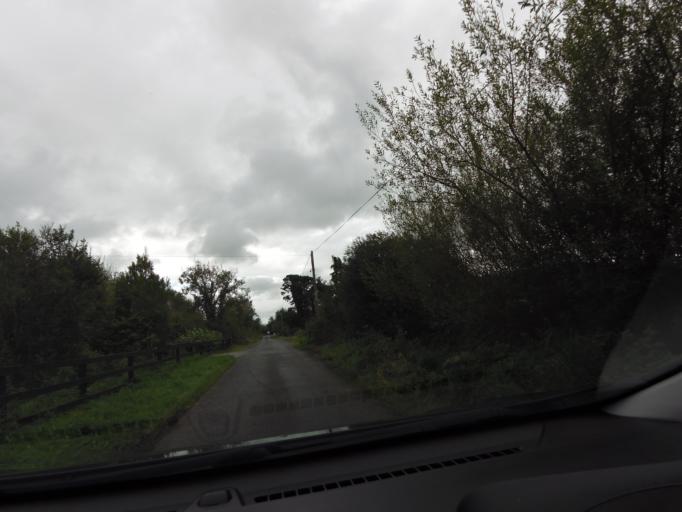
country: IE
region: Connaught
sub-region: County Galway
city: Loughrea
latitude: 53.2979
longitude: -8.5936
